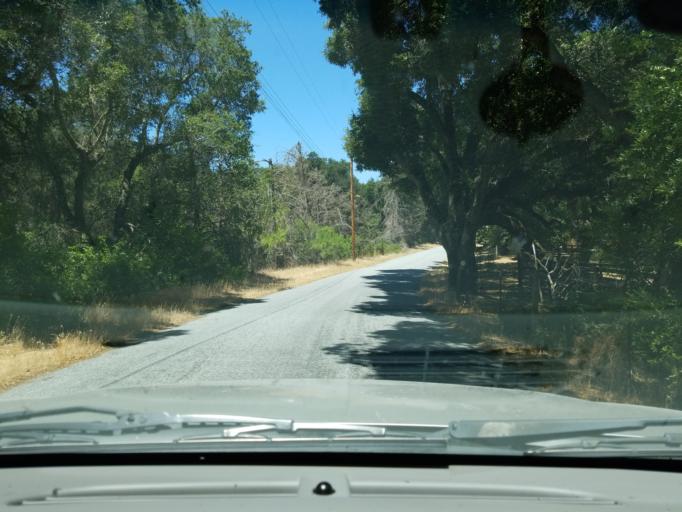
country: US
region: California
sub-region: Monterey County
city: Gonzales
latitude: 36.3798
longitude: -121.5728
